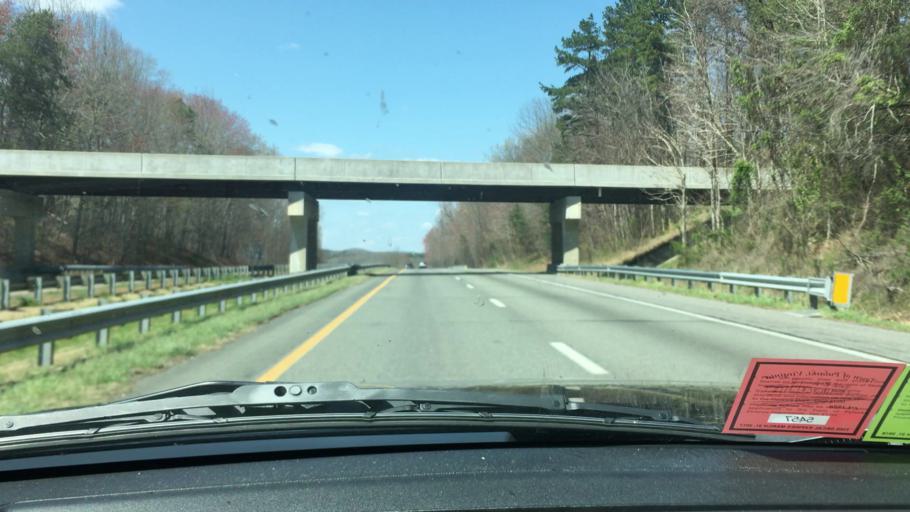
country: US
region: North Carolina
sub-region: Surry County
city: Pilot Mountain
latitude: 36.3881
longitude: -80.4900
